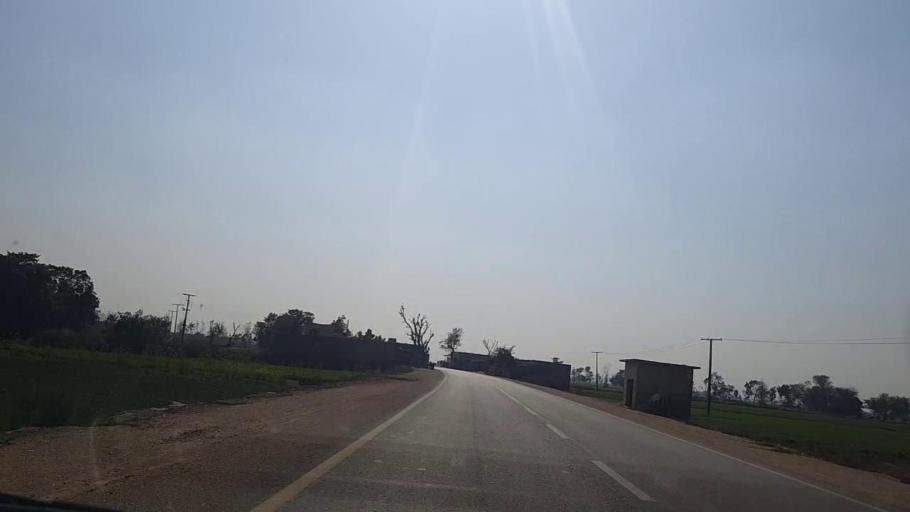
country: PK
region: Sindh
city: Sakrand
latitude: 26.0297
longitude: 68.3994
